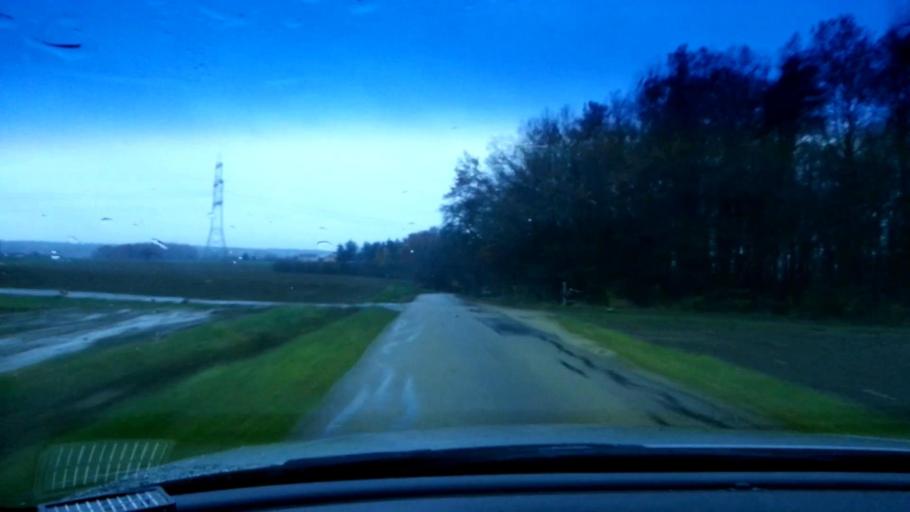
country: DE
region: Bavaria
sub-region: Upper Franconia
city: Memmelsdorf
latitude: 49.9482
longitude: 10.9498
